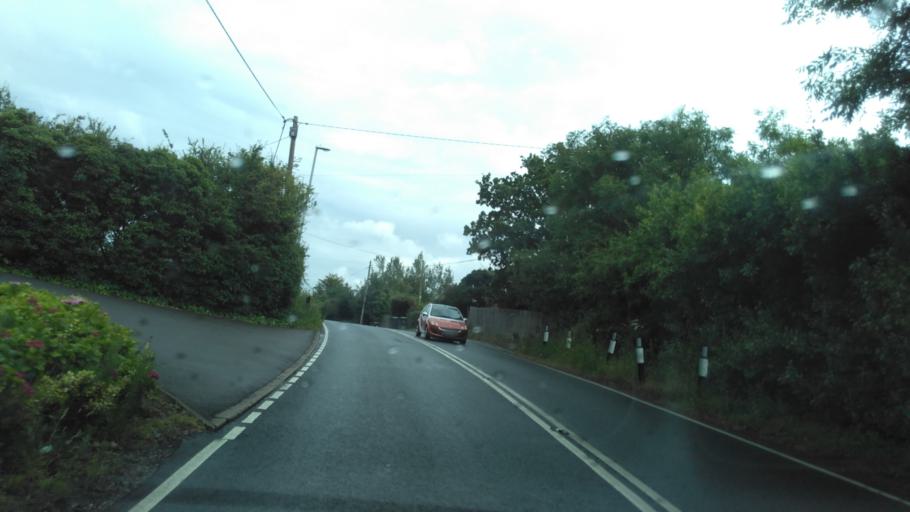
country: GB
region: England
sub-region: Kent
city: Blean
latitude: 51.3235
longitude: 1.0266
